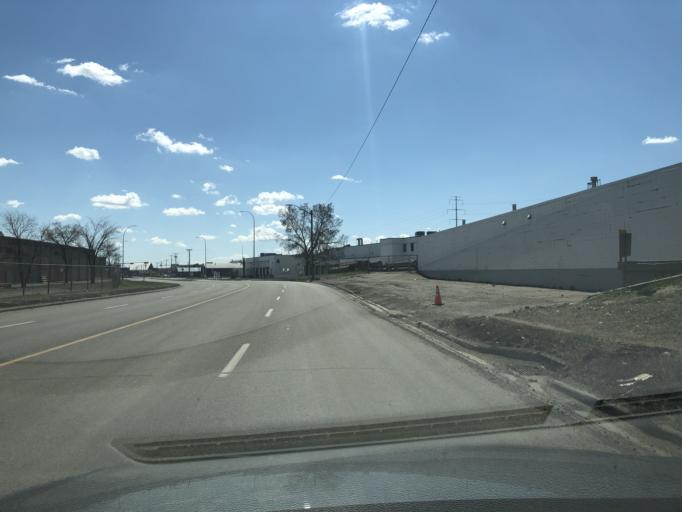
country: CA
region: Alberta
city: Calgary
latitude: 51.0224
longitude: -114.0310
